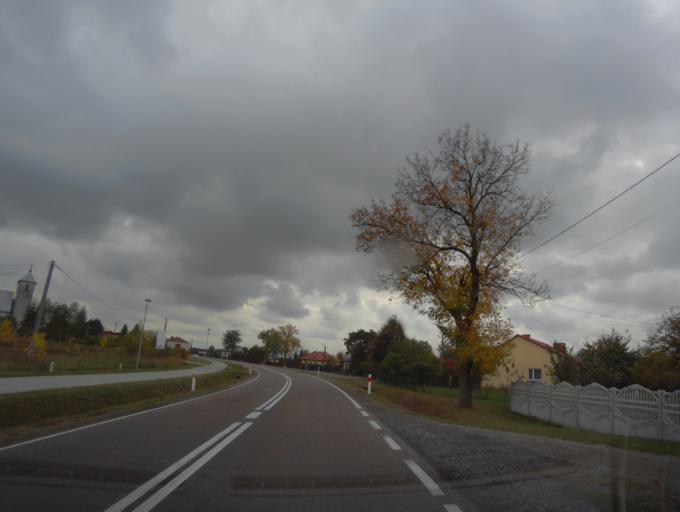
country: PL
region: Subcarpathian Voivodeship
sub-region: Powiat nizanski
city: Krzeszow
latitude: 50.3708
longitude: 22.3146
